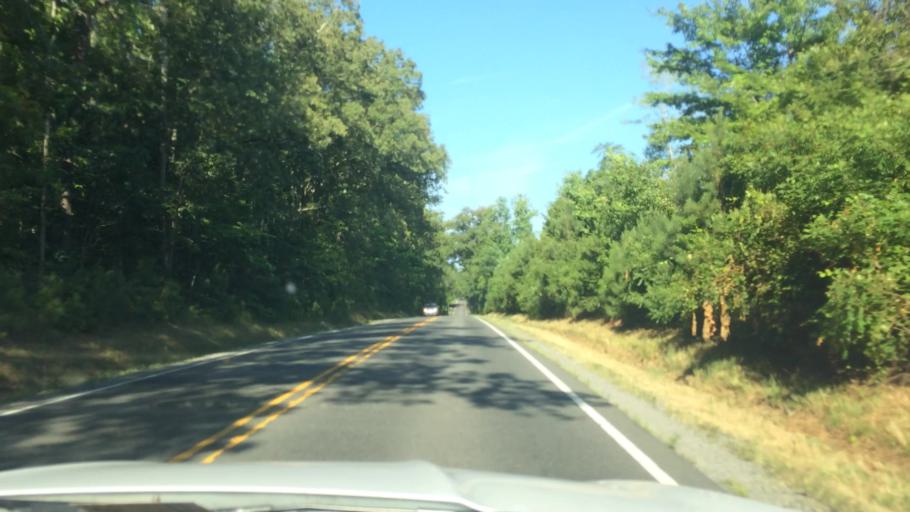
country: US
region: Virginia
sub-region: Lancaster County
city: Lancaster
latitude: 37.7694
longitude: -76.4857
